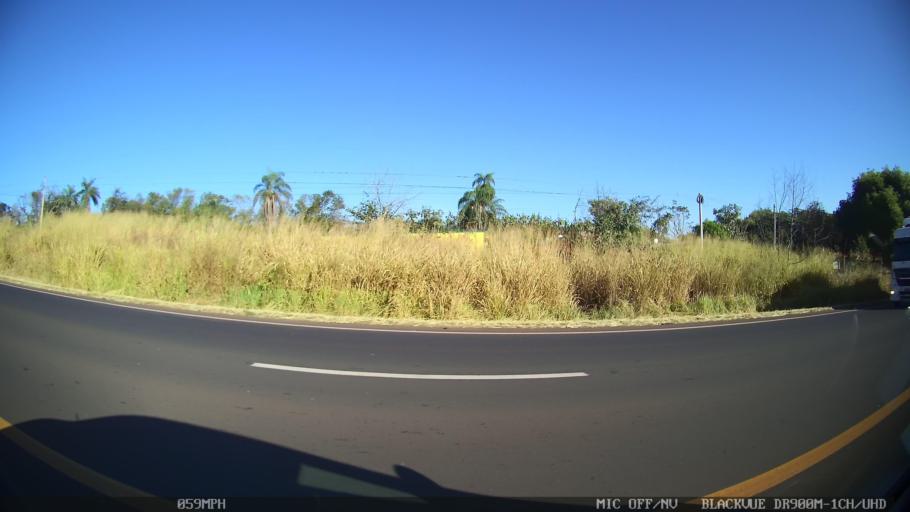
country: BR
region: Sao Paulo
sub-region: Olimpia
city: Olimpia
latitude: -20.7055
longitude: -48.9552
